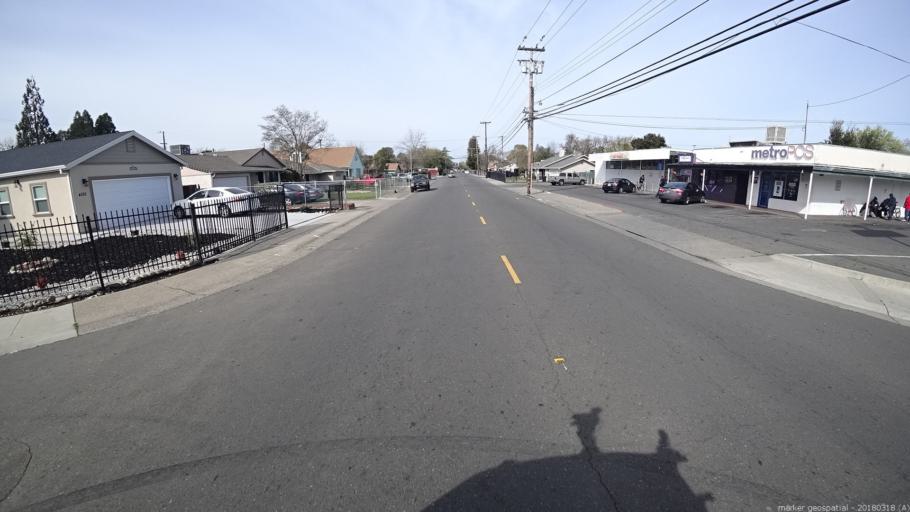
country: US
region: California
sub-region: Sacramento County
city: Parkway
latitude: 38.5322
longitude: -121.4577
